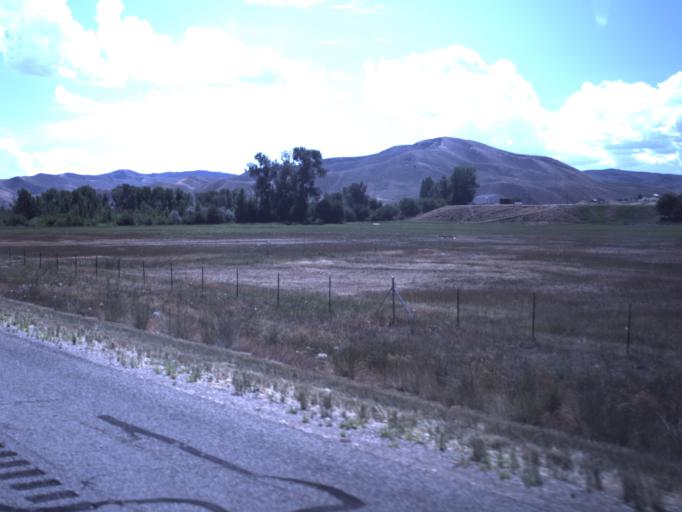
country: US
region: Utah
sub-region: Morgan County
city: Morgan
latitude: 41.0374
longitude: -111.5125
